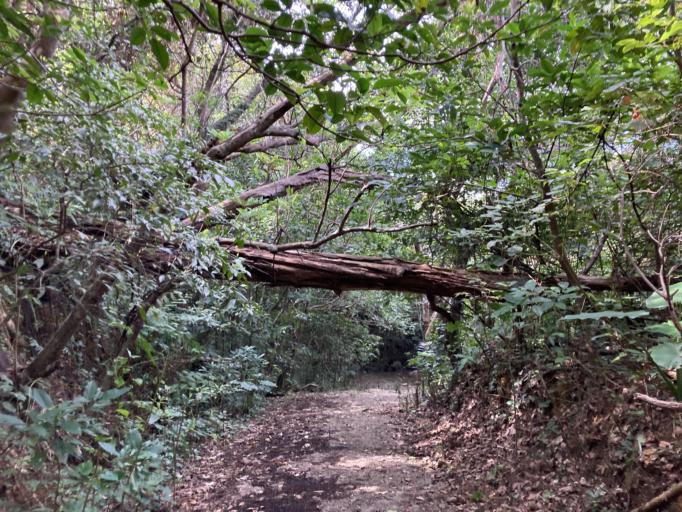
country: JP
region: Okinawa
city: Nago
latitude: 26.6887
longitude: 127.9278
